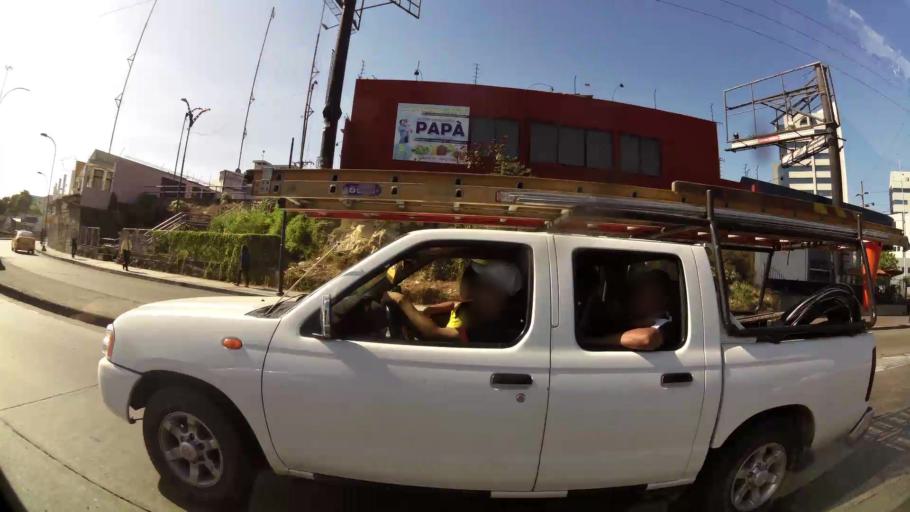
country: EC
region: Guayas
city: Eloy Alfaro
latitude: -2.1565
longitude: -79.8967
